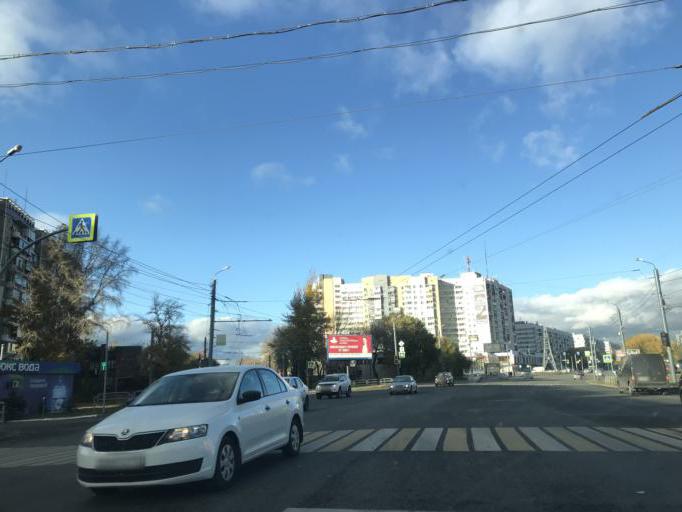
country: RU
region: Chelyabinsk
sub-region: Gorod Chelyabinsk
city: Chelyabinsk
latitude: 55.1700
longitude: 61.4530
